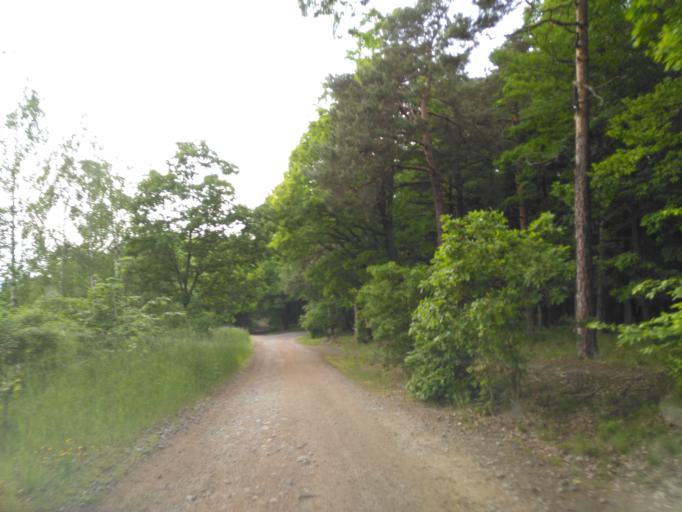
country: CZ
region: Plzensky
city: Zbiroh
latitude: 49.8576
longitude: 13.7446
